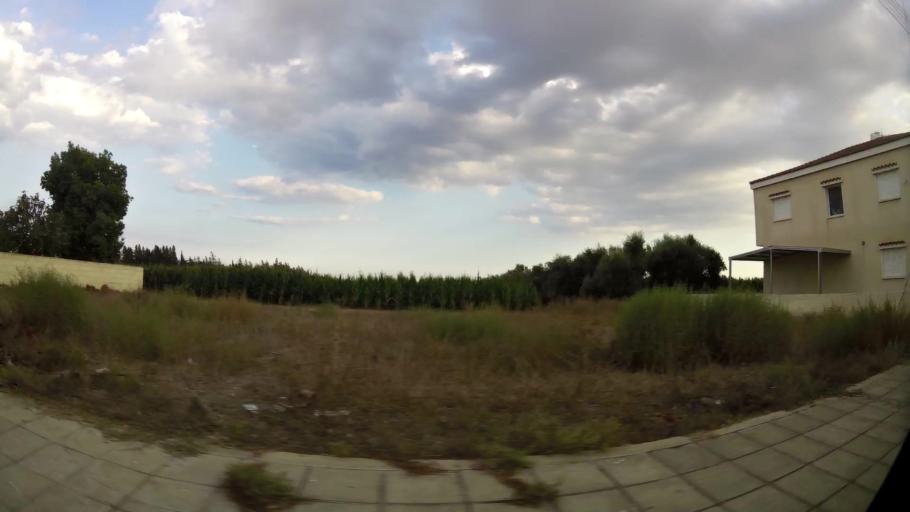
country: CY
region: Larnaka
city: Meneou
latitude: 34.8566
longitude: 33.5877
